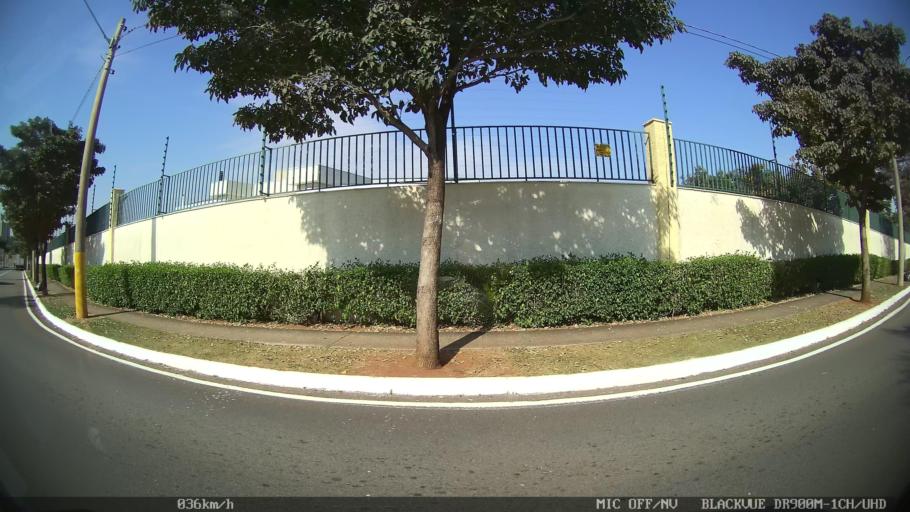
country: BR
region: Sao Paulo
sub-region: Paulinia
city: Paulinia
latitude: -22.7760
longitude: -47.1508
